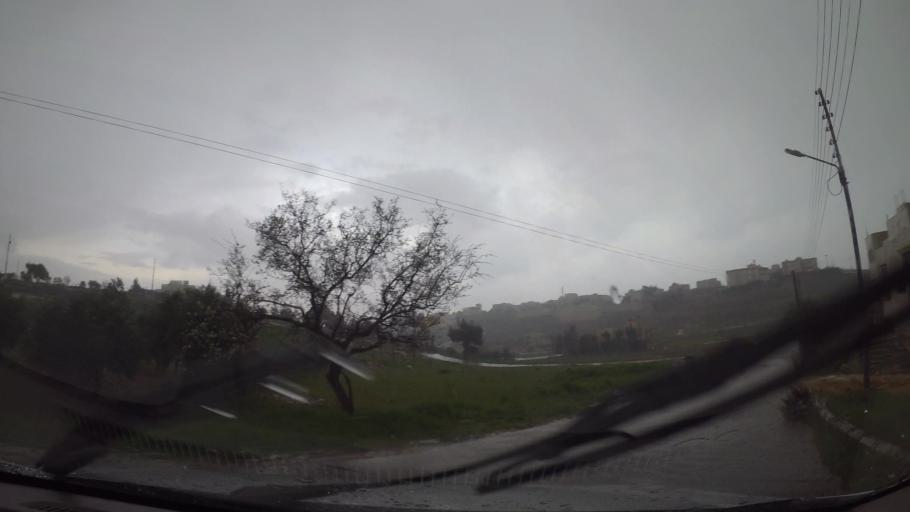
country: JO
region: Amman
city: Umm as Summaq
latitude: 31.8792
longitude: 35.8631
